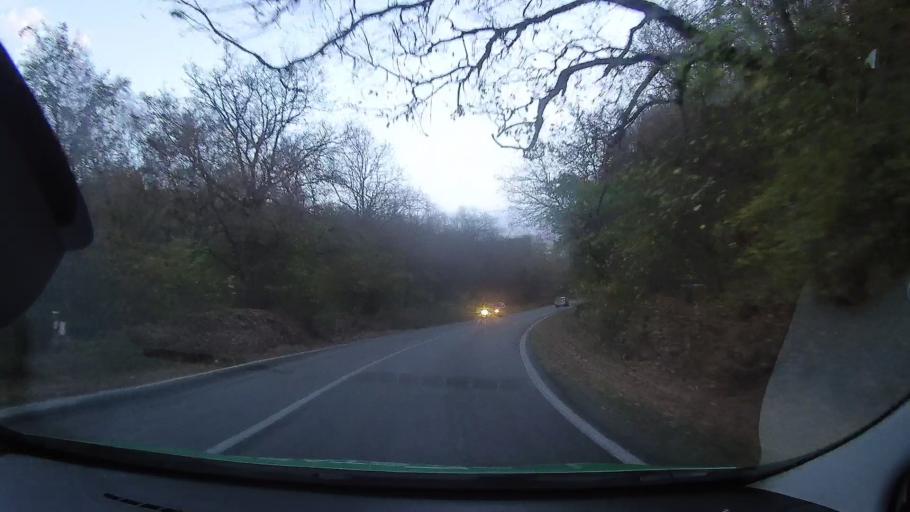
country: RO
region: Constanta
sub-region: Comuna Lipnita
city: Lipnita
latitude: 44.0943
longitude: 27.6533
